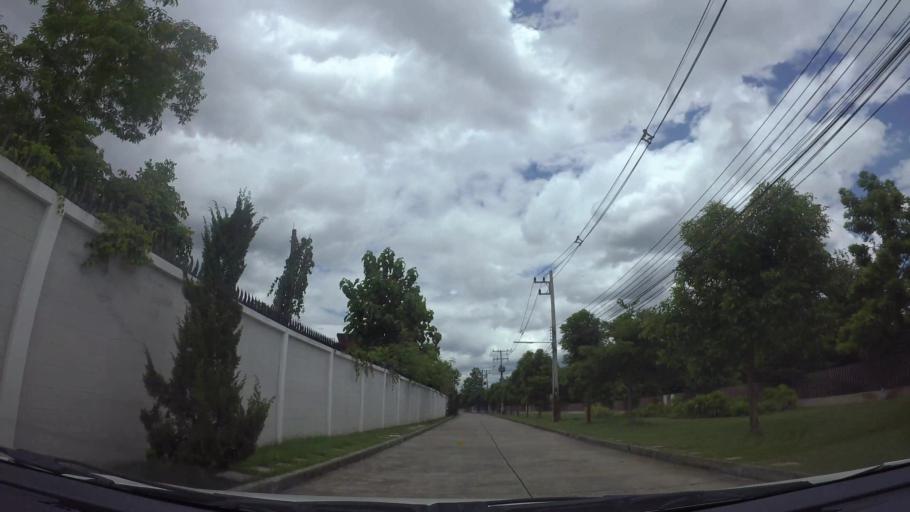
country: TH
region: Chiang Mai
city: Saraphi
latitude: 18.7469
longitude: 99.0378
